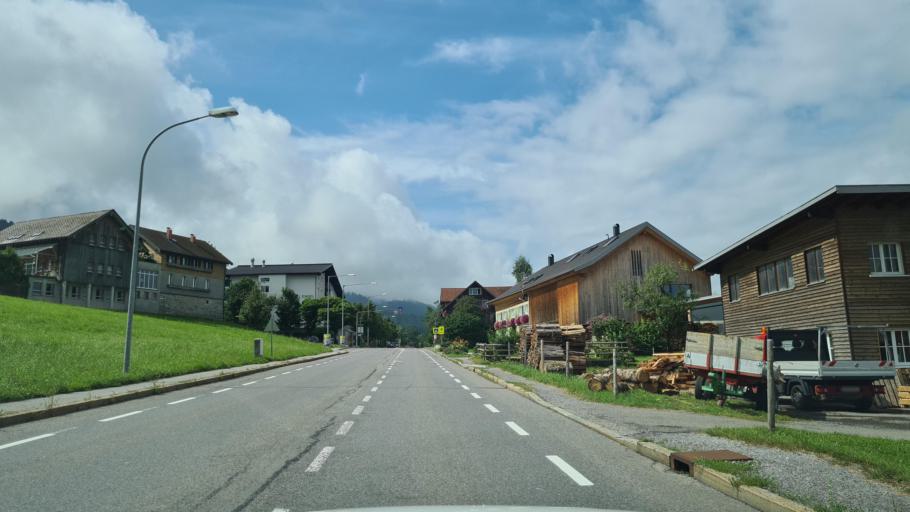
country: AT
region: Vorarlberg
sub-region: Politischer Bezirk Bregenz
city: Doren
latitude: 47.4594
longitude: 9.8515
